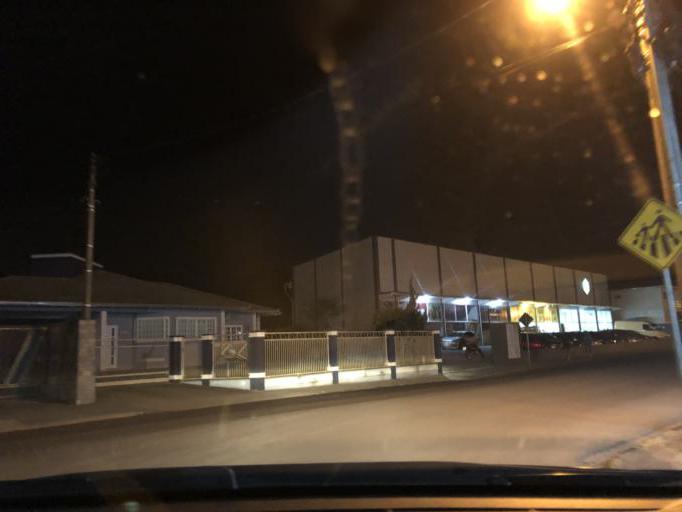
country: BR
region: Santa Catarina
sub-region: Jaragua Do Sul
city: Jaragua do Sul
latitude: -26.5085
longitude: -49.1339
